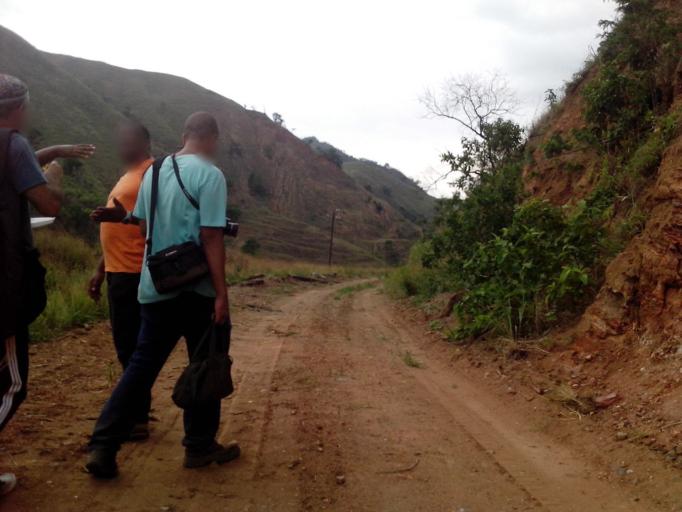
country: BR
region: Rio de Janeiro
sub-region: Miguel Pereira
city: Miguel Pereira
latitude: -22.5027
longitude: -43.5005
